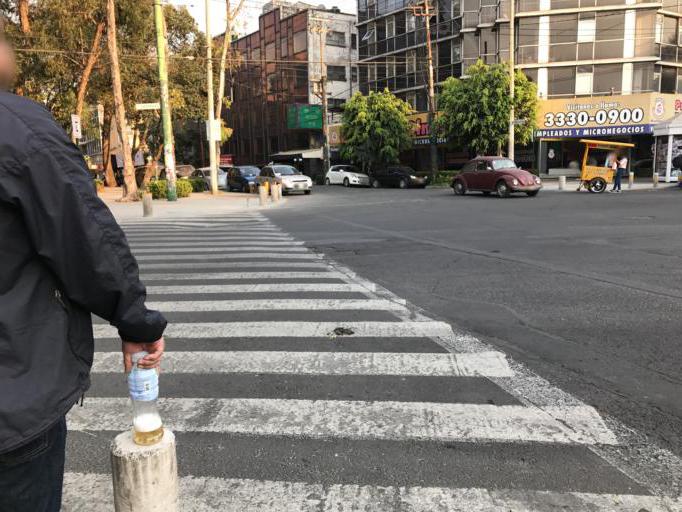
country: MX
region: Mexico City
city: Benito Juarez
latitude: 19.3926
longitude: -99.1508
